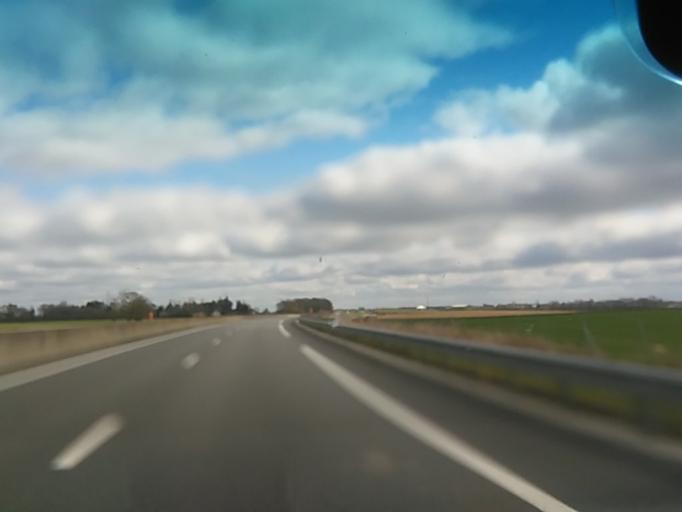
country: FR
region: Haute-Normandie
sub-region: Departement de l'Eure
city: Bernay
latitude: 49.1399
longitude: 0.5538
